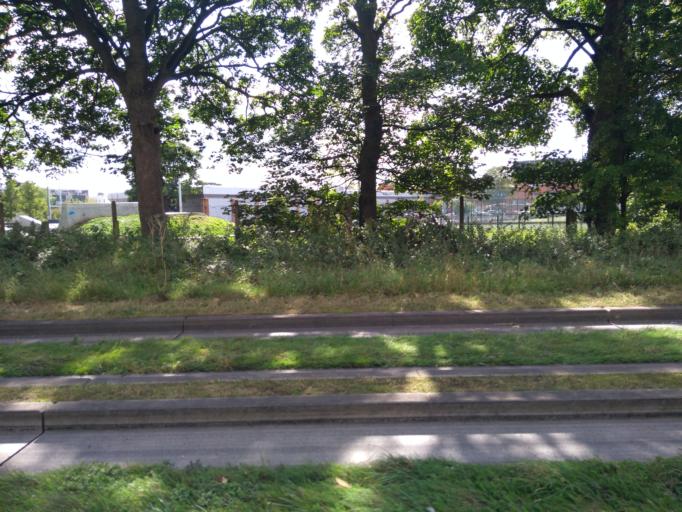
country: GB
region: England
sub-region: Central Bedfordshire
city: Dunstable
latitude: 51.8927
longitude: -0.5200
